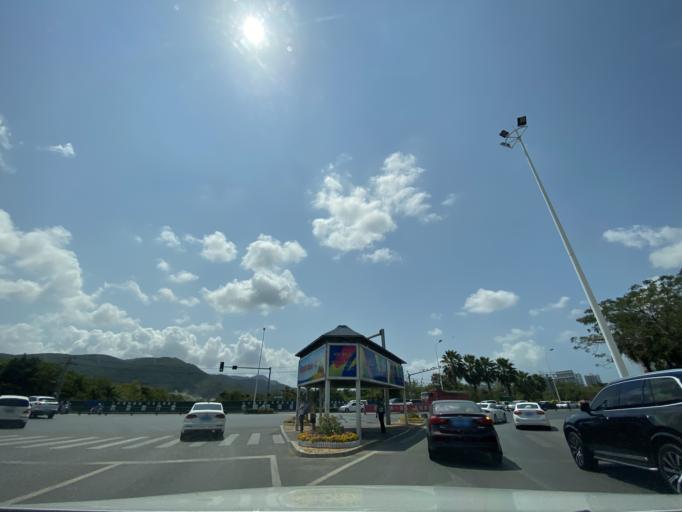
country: CN
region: Hainan
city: Tiandu
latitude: 18.2930
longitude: 109.5293
